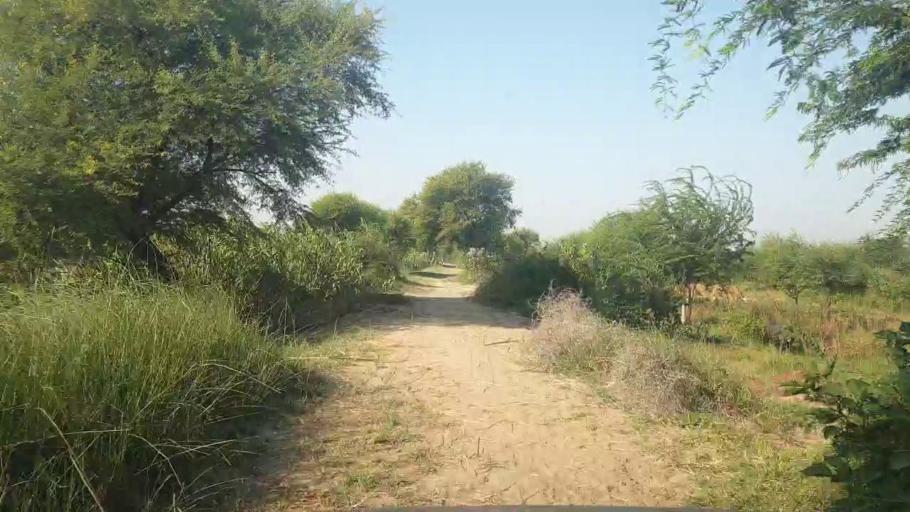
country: PK
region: Sindh
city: Badin
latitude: 24.7124
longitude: 68.8958
